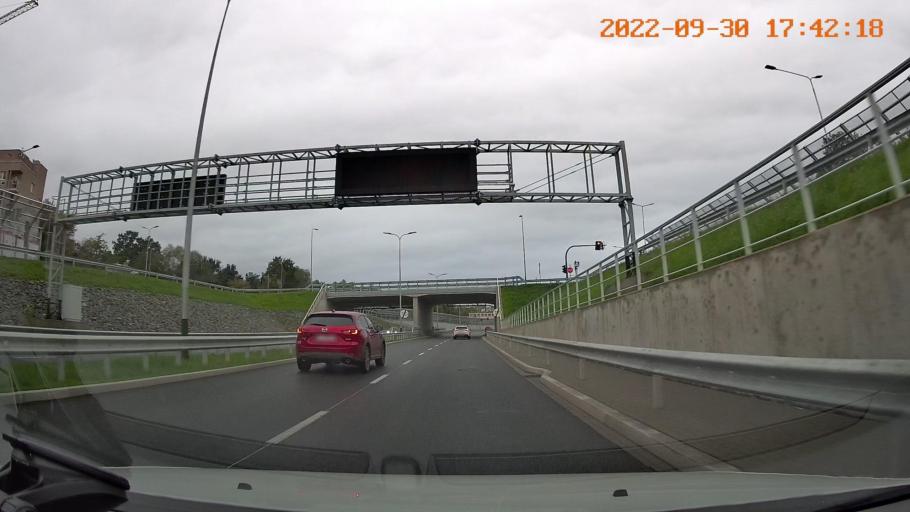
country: PL
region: Lesser Poland Voivodeship
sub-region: Krakow
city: Krakow
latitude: 50.0242
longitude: 19.9206
